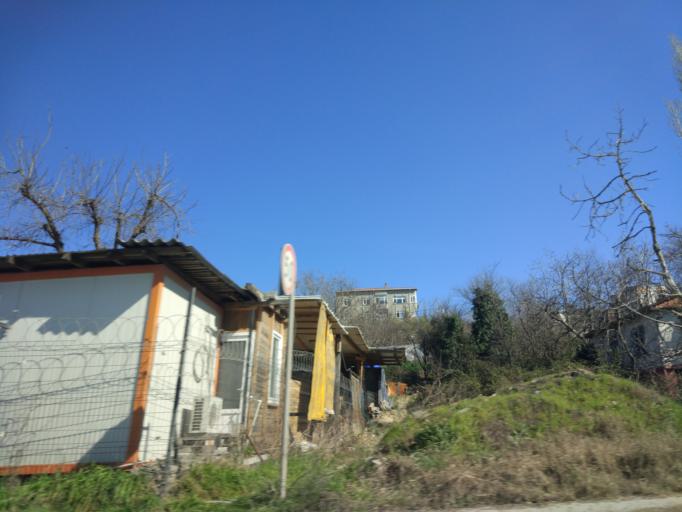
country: TR
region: Istanbul
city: Basaksehir
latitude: 41.0527
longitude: 28.7498
